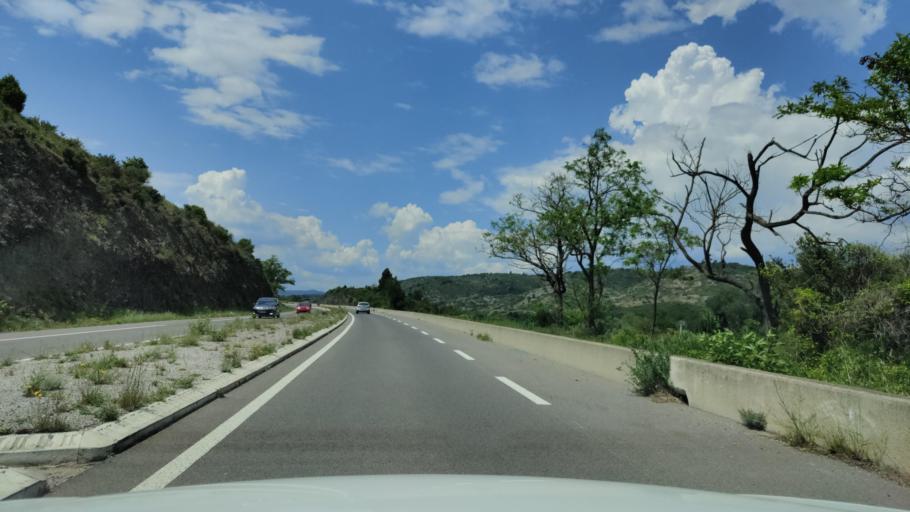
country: FR
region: Languedoc-Roussillon
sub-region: Departement des Pyrenees-Orientales
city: Estagel
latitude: 42.7757
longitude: 2.7382
